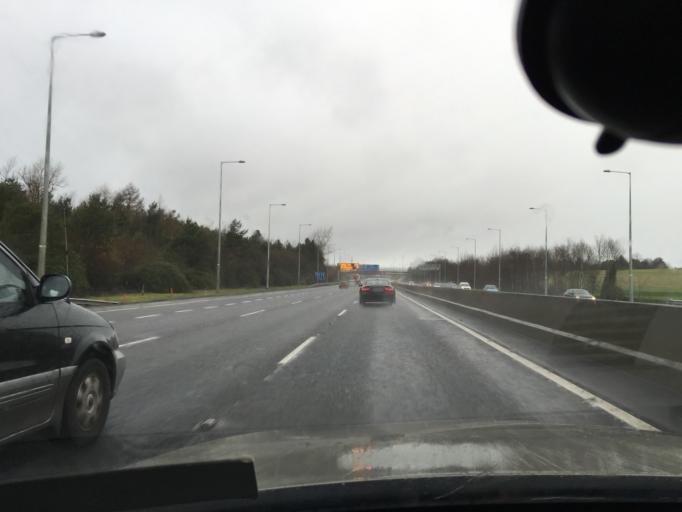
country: IE
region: Leinster
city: Firhouse
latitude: 53.3023
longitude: -6.3437
